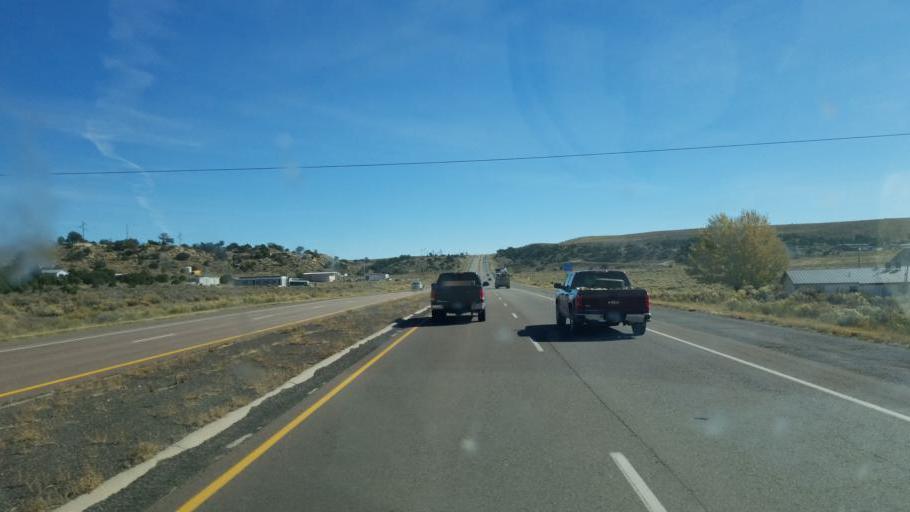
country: US
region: Arizona
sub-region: Apache County
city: Window Rock
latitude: 35.6390
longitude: -109.0066
